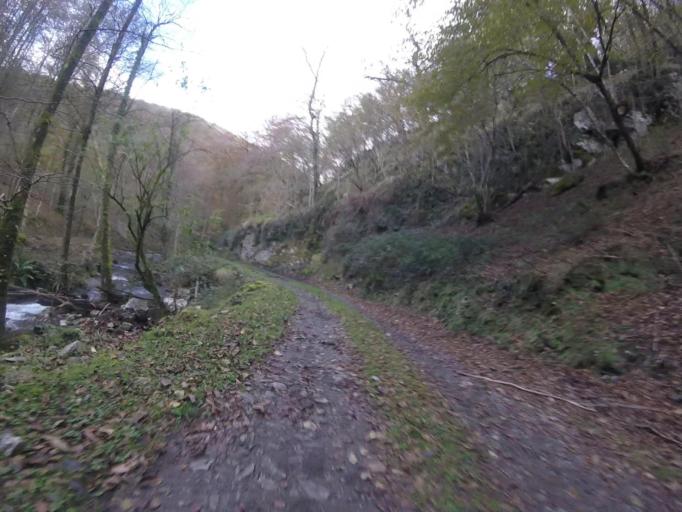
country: ES
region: Navarre
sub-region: Provincia de Navarra
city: Goizueta
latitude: 43.1847
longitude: -1.7996
